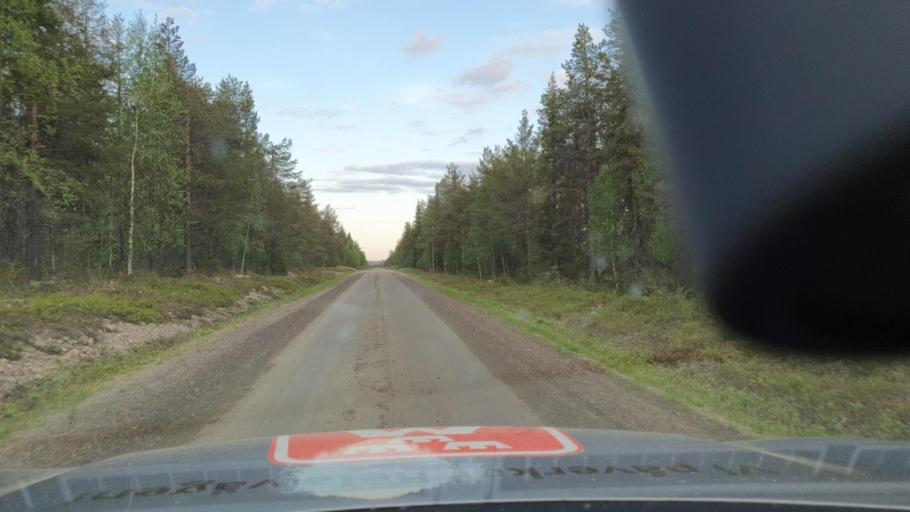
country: SE
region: Norrbotten
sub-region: Bodens Kommun
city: Boden
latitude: 66.5896
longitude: 21.3845
